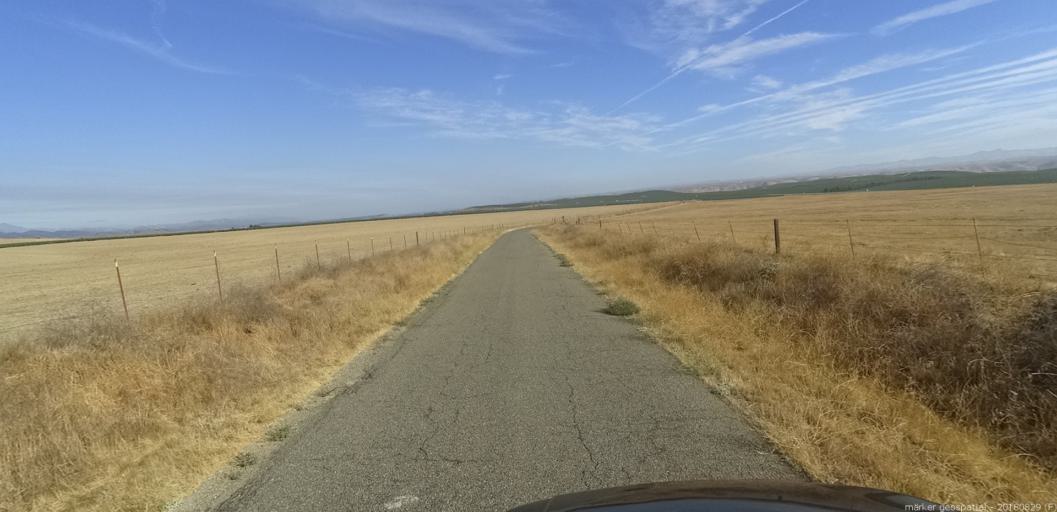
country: US
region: California
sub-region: Monterey County
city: King City
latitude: 36.0513
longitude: -120.9786
